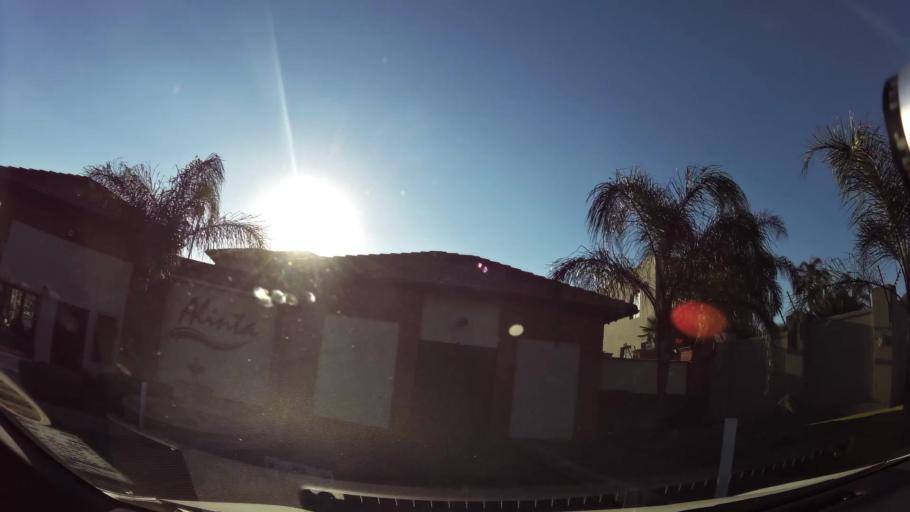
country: ZA
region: Gauteng
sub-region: City of Johannesburg Metropolitan Municipality
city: Johannesburg
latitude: -26.2889
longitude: 28.0714
